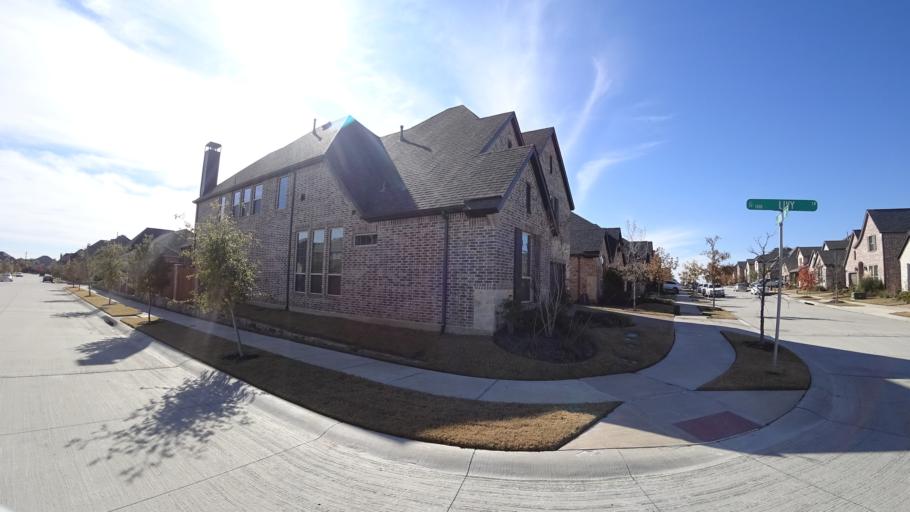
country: US
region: Texas
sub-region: Denton County
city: The Colony
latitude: 33.0267
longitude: -96.8953
